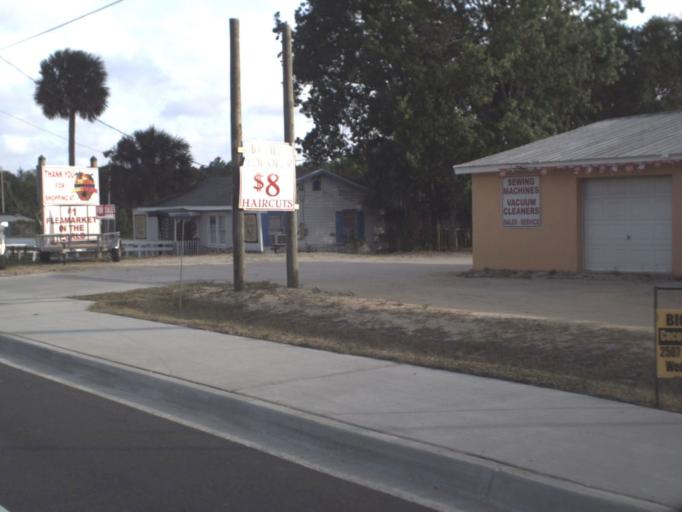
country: US
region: Florida
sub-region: Brevard County
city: Cocoa
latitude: 28.3936
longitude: -80.7487
